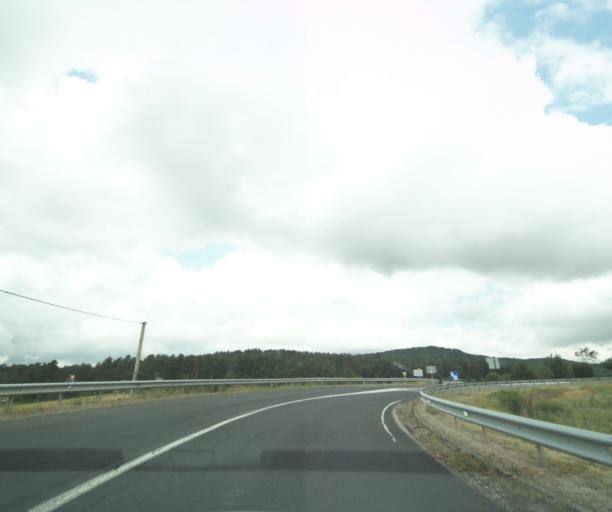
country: FR
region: Midi-Pyrenees
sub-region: Departement de l'Aveyron
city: Severac-le-Chateau
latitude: 44.3842
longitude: 3.1160
